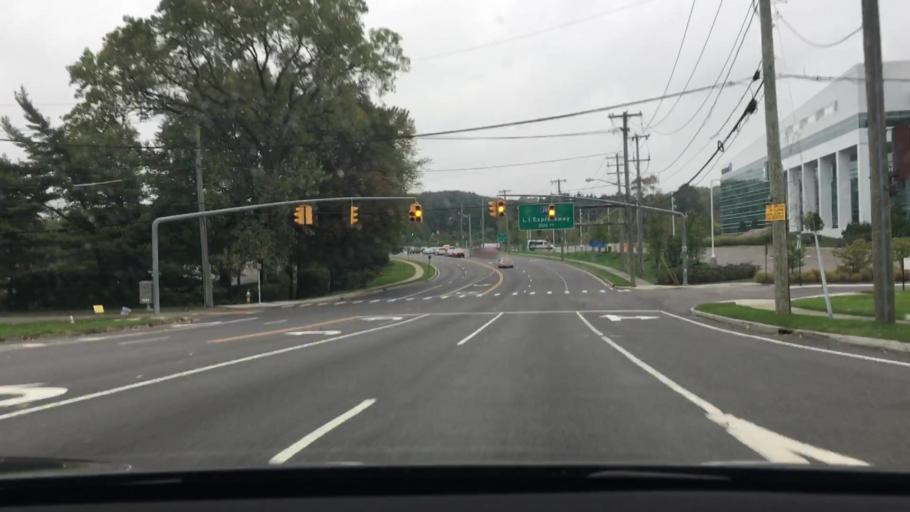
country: US
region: New York
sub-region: Nassau County
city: Manhasset Hills
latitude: 40.7664
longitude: -73.6904
